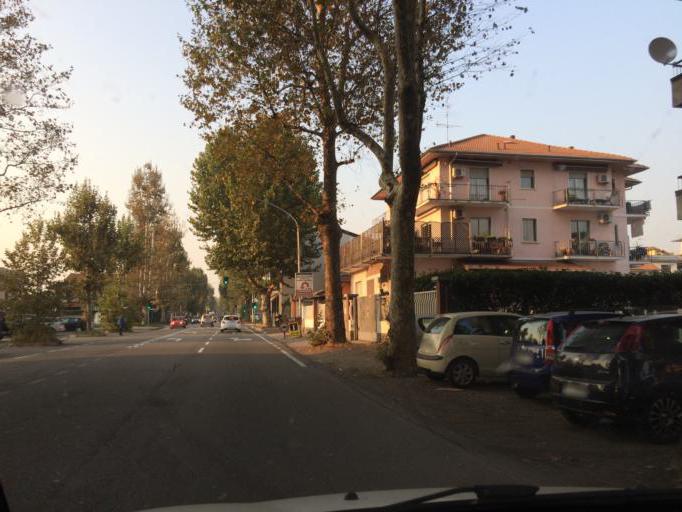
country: IT
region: Lombardy
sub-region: Provincia di Varese
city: Castellanza
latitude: 45.6064
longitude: 8.8910
